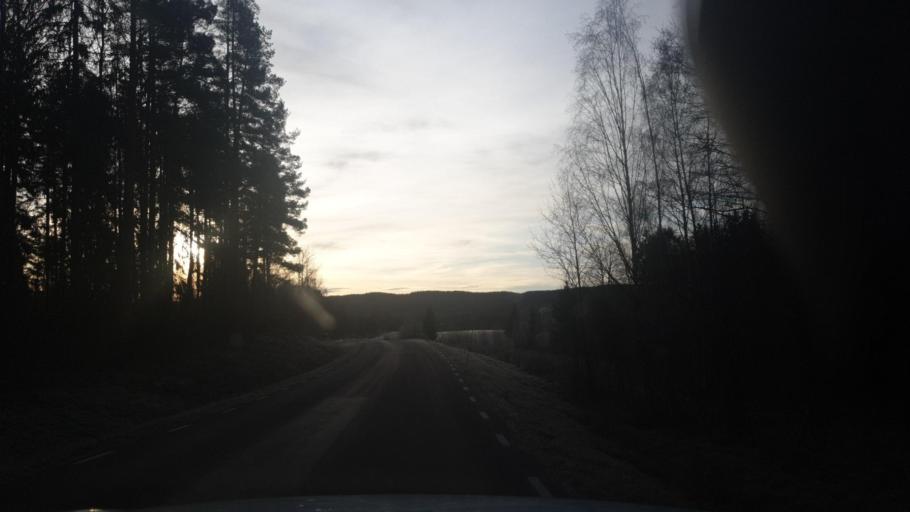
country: SE
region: Vaermland
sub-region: Arvika Kommun
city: Arvika
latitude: 59.5309
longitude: 12.8243
